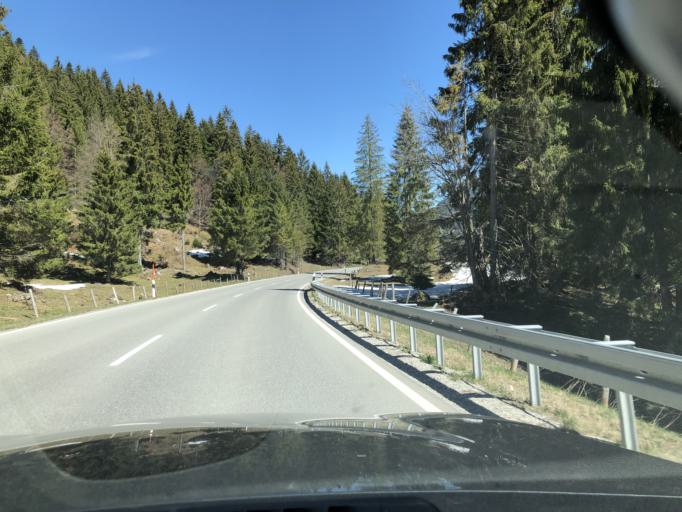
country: AT
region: Tyrol
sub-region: Politischer Bezirk Reutte
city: Schattwald
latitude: 47.5228
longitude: 10.4107
